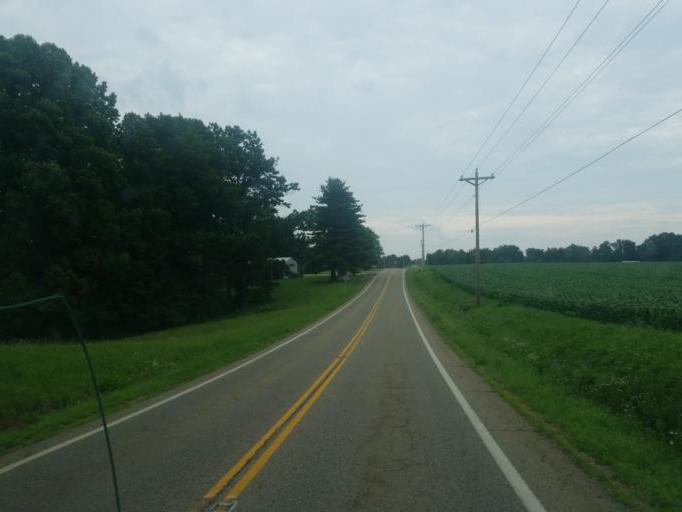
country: US
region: Ohio
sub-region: Carroll County
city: Lake Mohawk
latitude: 40.6323
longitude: -81.2037
